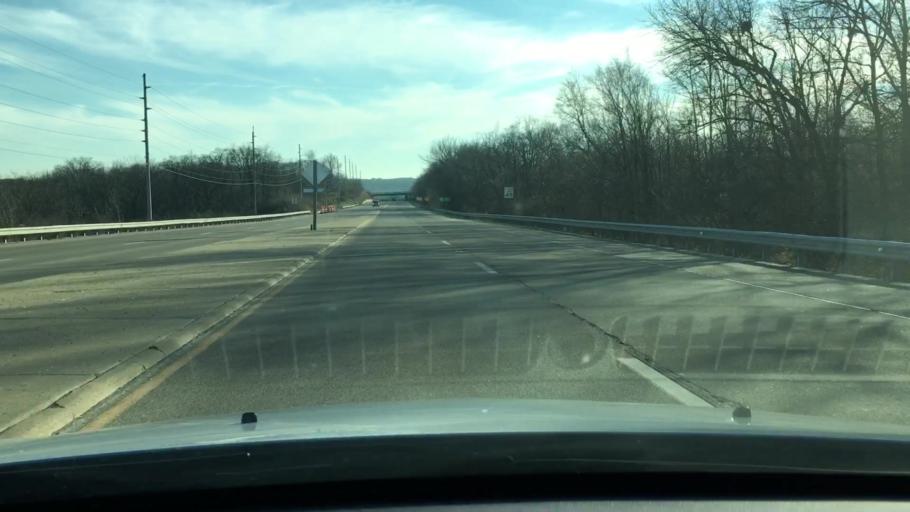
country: US
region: Illinois
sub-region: LaSalle County
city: Peru
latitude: 41.3360
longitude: -89.1201
